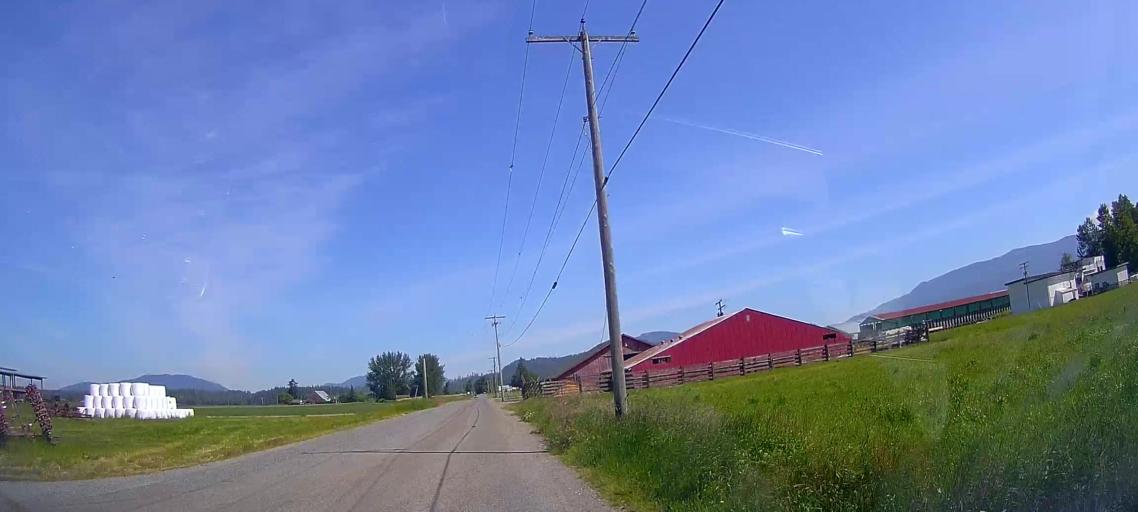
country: US
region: Washington
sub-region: Skagit County
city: Burlington
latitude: 48.5018
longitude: -122.3075
